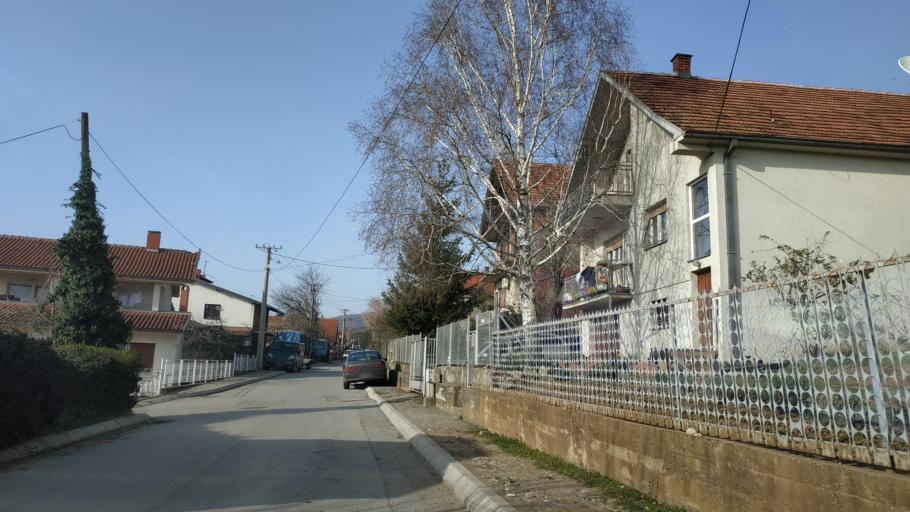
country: RS
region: Central Serbia
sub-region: Nisavski Okrug
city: Aleksinac
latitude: 43.5427
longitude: 21.7169
